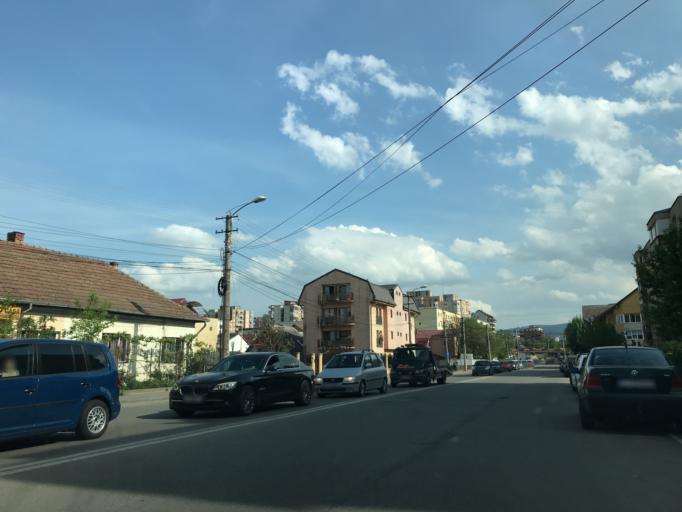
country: RO
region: Cluj
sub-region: Municipiul Cluj-Napoca
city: Cluj-Napoca
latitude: 46.7820
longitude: 23.6192
